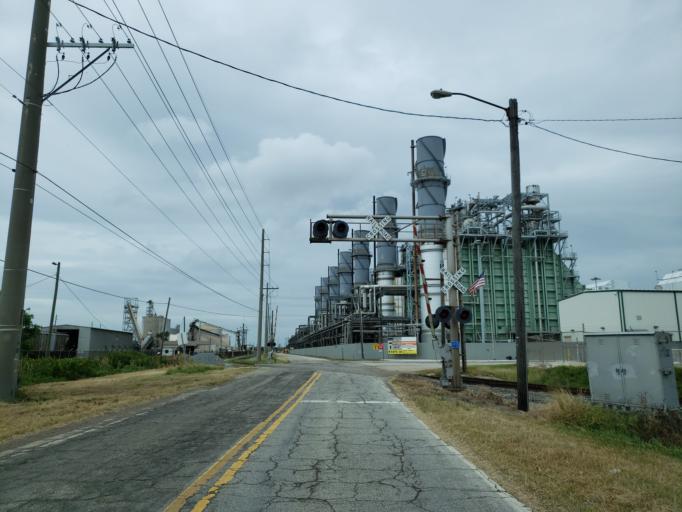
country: US
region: Florida
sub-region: Hillsborough County
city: Palm River-Clair Mel
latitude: 27.9063
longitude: -82.4156
